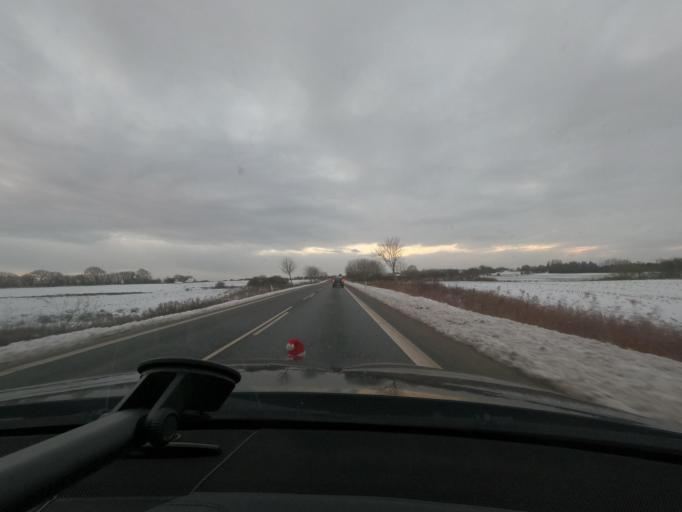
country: DK
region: South Denmark
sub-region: Aabenraa Kommune
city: Krusa
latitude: 54.8763
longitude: 9.4696
